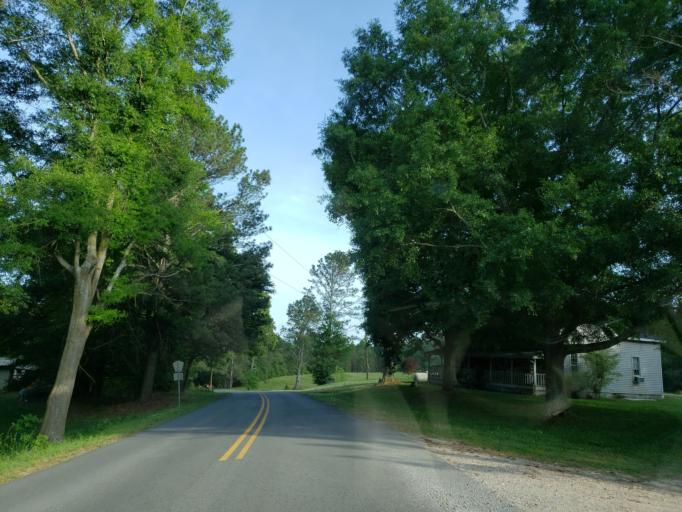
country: US
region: Georgia
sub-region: Carroll County
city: Bowdon
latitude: 33.4936
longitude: -85.3100
